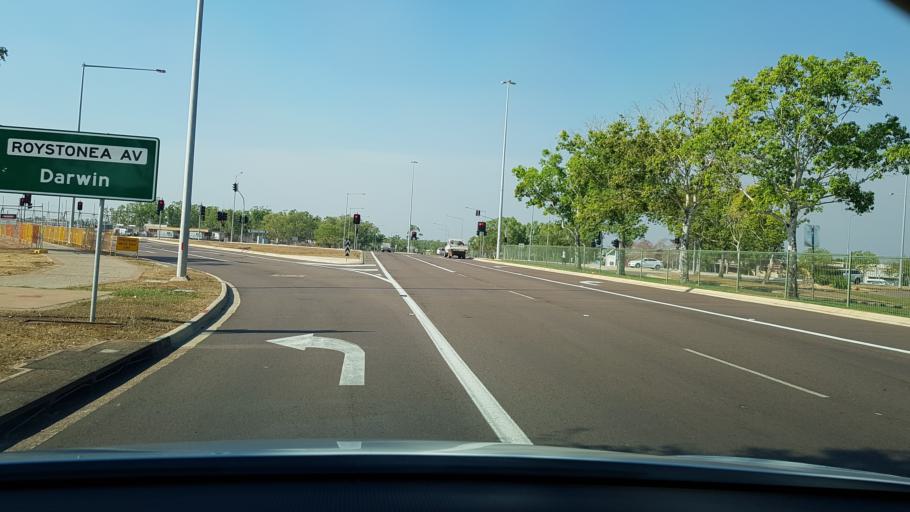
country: AU
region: Northern Territory
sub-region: Palmerston
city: Palmerston
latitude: -12.4799
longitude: 130.9877
